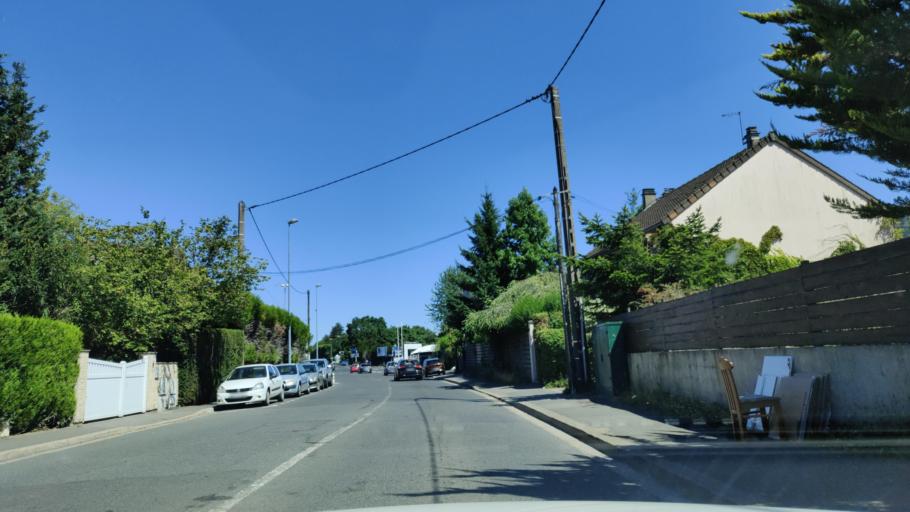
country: FR
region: Ile-de-France
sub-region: Departement de l'Essonne
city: Orsay
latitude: 48.6844
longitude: 2.1866
